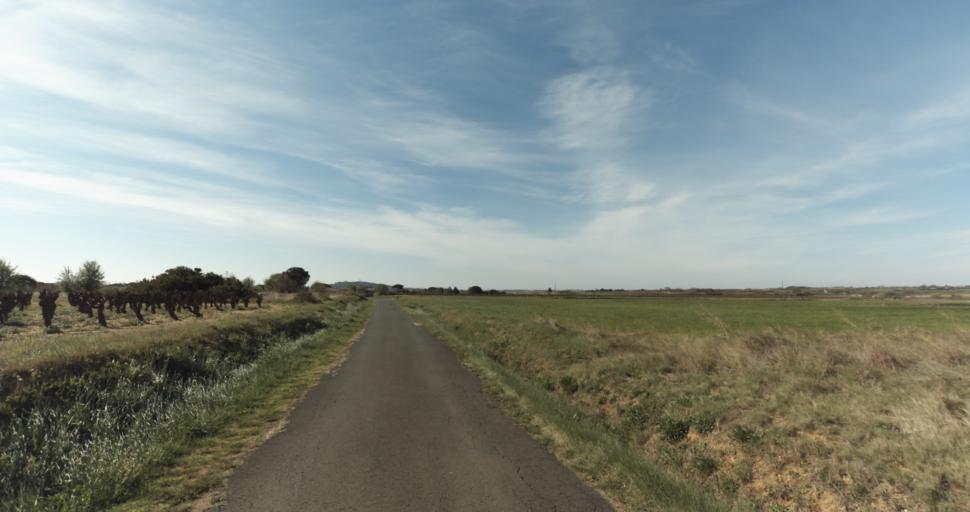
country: FR
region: Languedoc-Roussillon
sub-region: Departement de l'Herault
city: Marseillan
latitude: 43.3413
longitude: 3.5180
